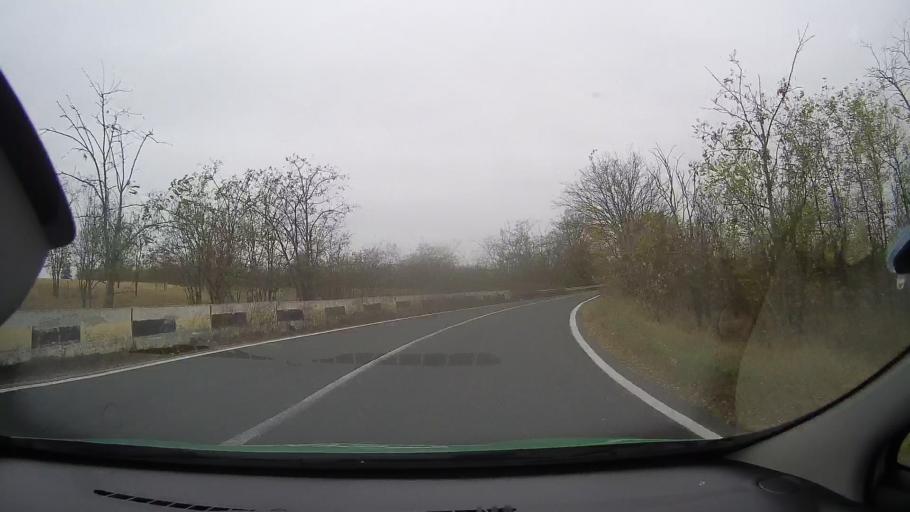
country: RO
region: Constanta
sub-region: Comuna Saraiu
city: Saraiu
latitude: 44.7129
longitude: 28.1266
